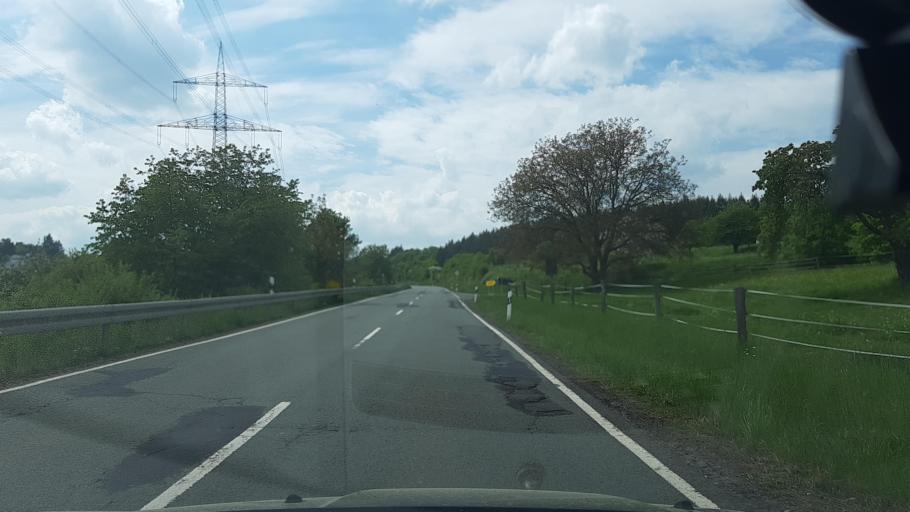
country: DE
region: Hesse
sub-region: Regierungsbezirk Giessen
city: Greifenstein
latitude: 50.6069
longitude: 8.3202
